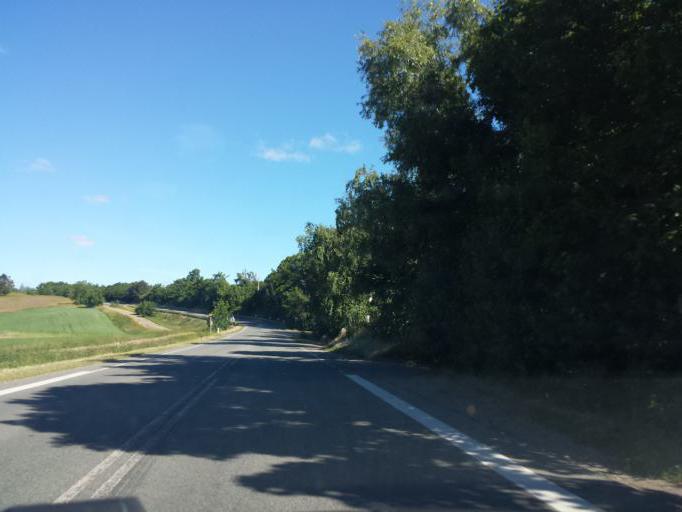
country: DK
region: Capital Region
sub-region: Egedal Kommune
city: Ganlose
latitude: 55.7770
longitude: 12.2919
